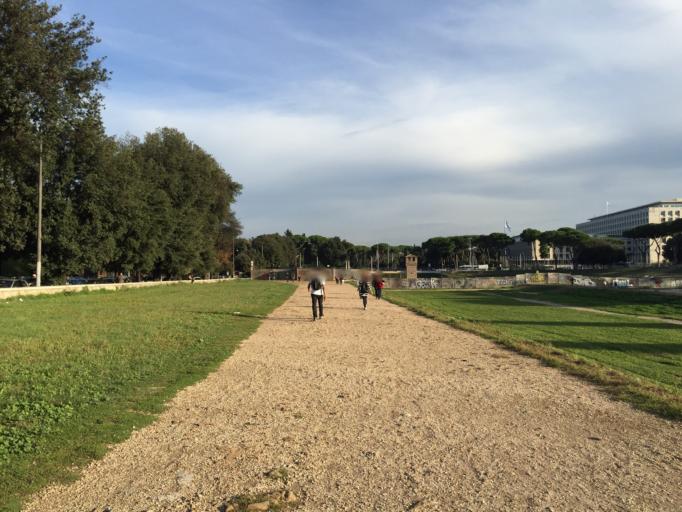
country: IT
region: Latium
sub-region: Citta metropolitana di Roma Capitale
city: Rome
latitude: 41.8863
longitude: 12.4862
